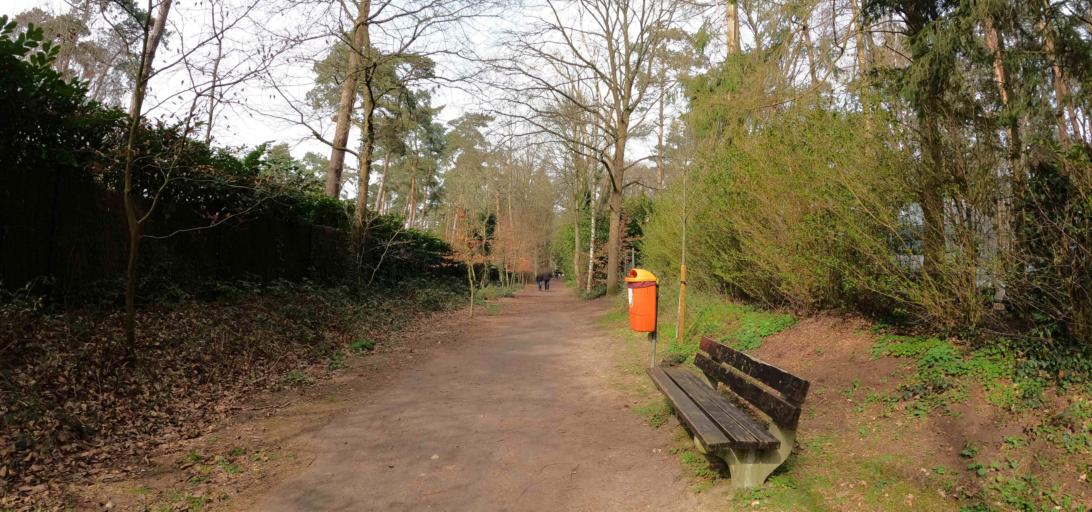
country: BE
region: Flanders
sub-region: Provincie Oost-Vlaanderen
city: Waasmunster
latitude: 51.1245
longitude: 4.0907
